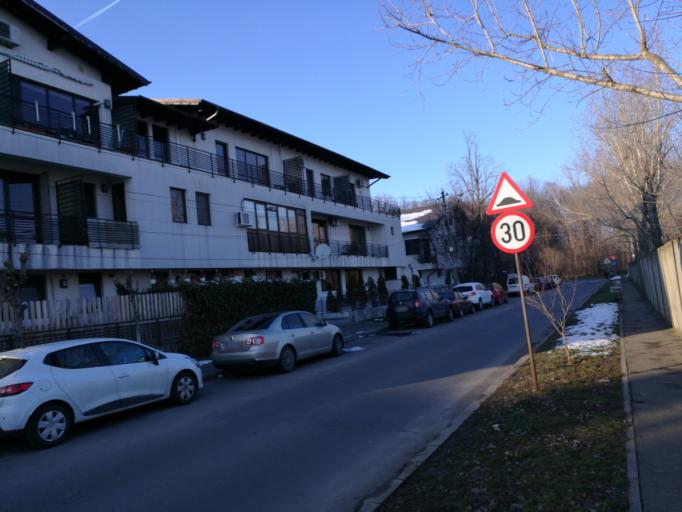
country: RO
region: Ilfov
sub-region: Comuna Otopeni
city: Otopeni
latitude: 44.5077
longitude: 26.0602
